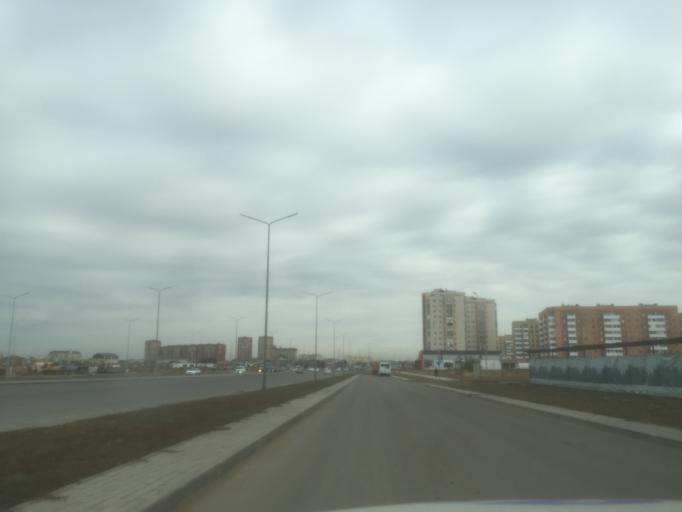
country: KZ
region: Astana Qalasy
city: Astana
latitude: 51.1684
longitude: 71.3763
